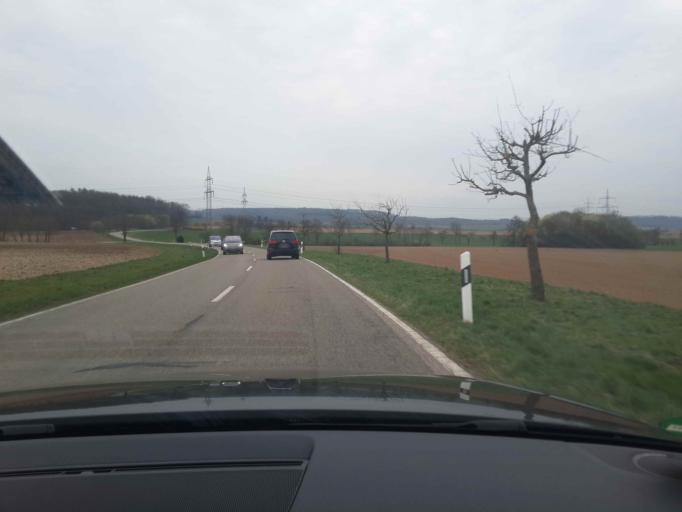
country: DE
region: Baden-Wuerttemberg
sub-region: Regierungsbezirk Stuttgart
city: Oedheim
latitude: 49.2335
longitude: 9.2666
